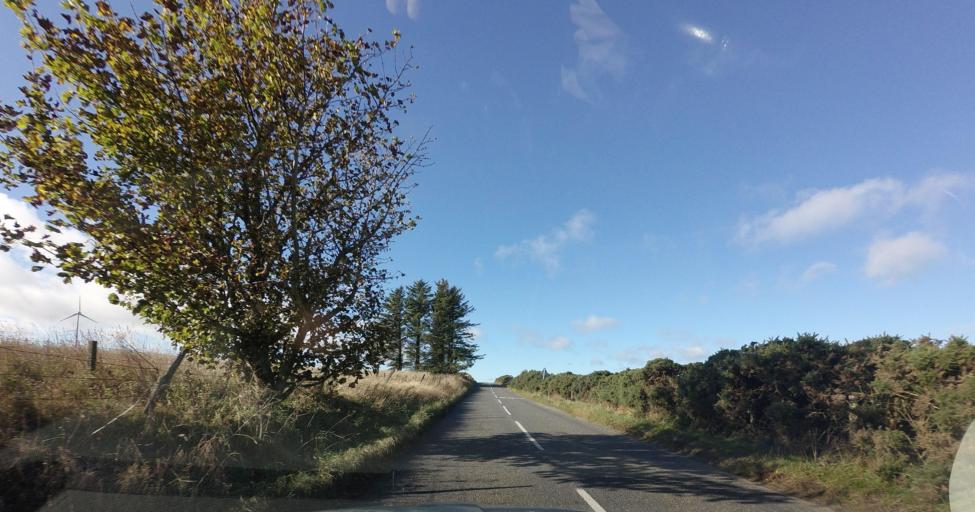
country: GB
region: Scotland
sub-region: Aberdeenshire
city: Macduff
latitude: 57.6612
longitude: -2.3619
